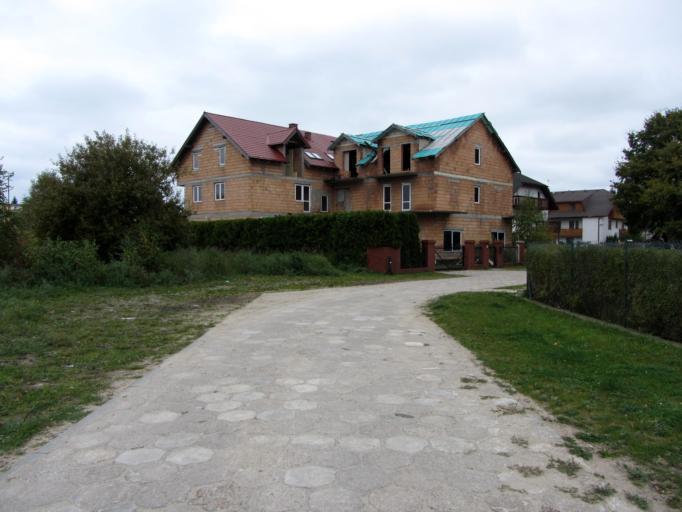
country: PL
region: West Pomeranian Voivodeship
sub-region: Powiat kolobrzeski
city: Kolobrzeg
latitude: 54.1719
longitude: 15.5500
